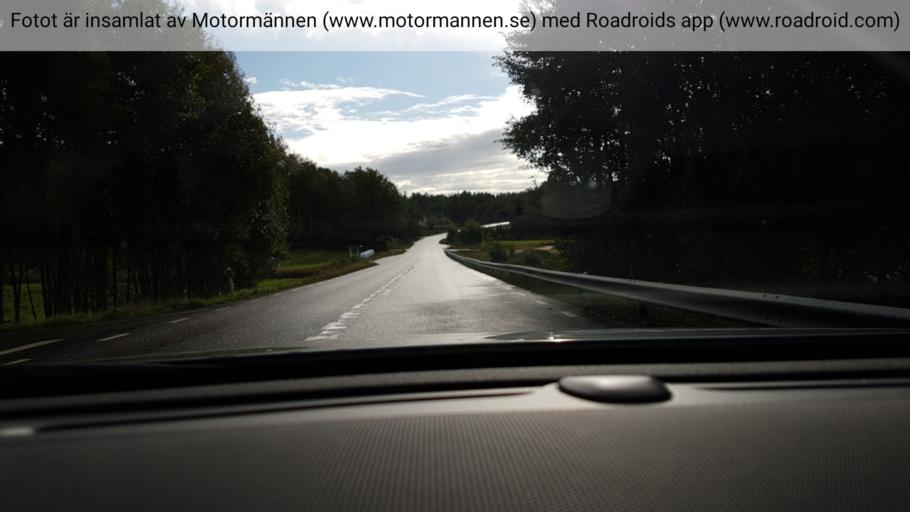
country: SE
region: Vaestra Goetaland
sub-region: Harryda Kommun
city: Ravlanda
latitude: 57.5788
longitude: 12.4977
